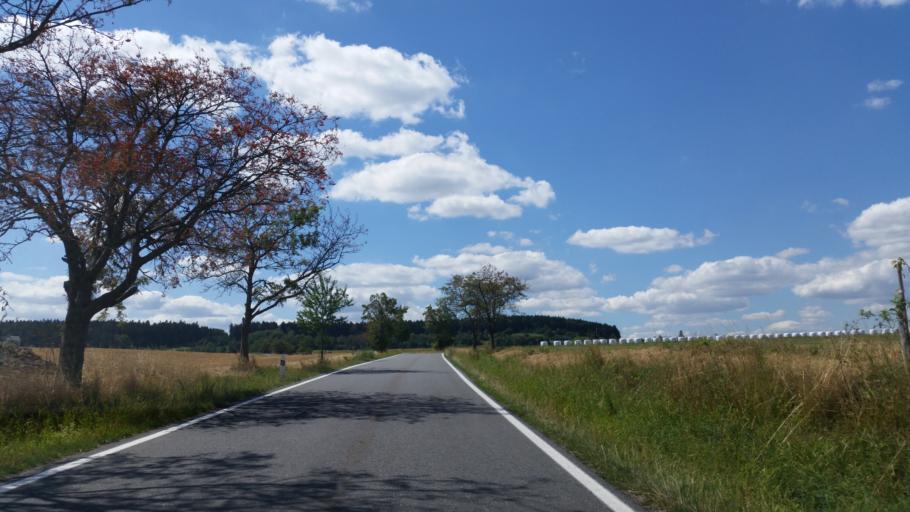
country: CZ
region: Vysocina
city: Lipa
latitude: 49.4987
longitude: 15.5312
